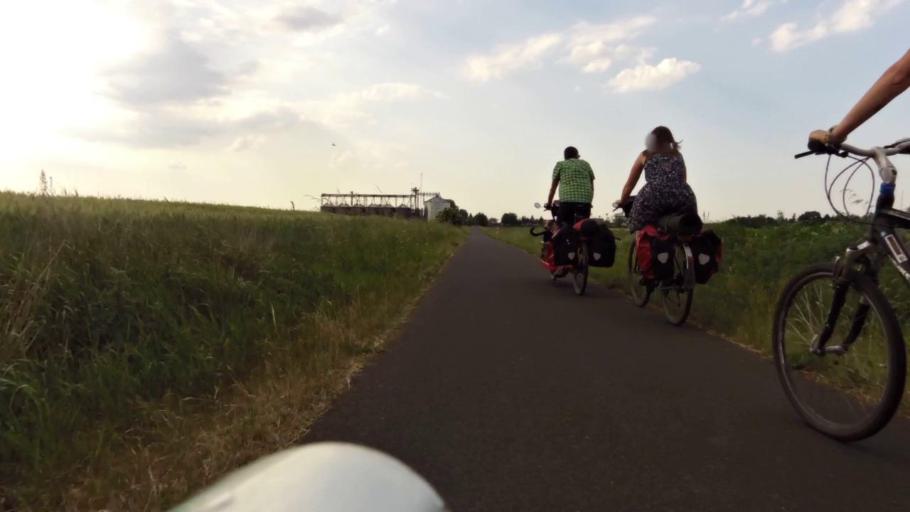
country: PL
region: Kujawsko-Pomorskie
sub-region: Powiat torunski
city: Lubianka
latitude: 53.1285
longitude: 18.4657
